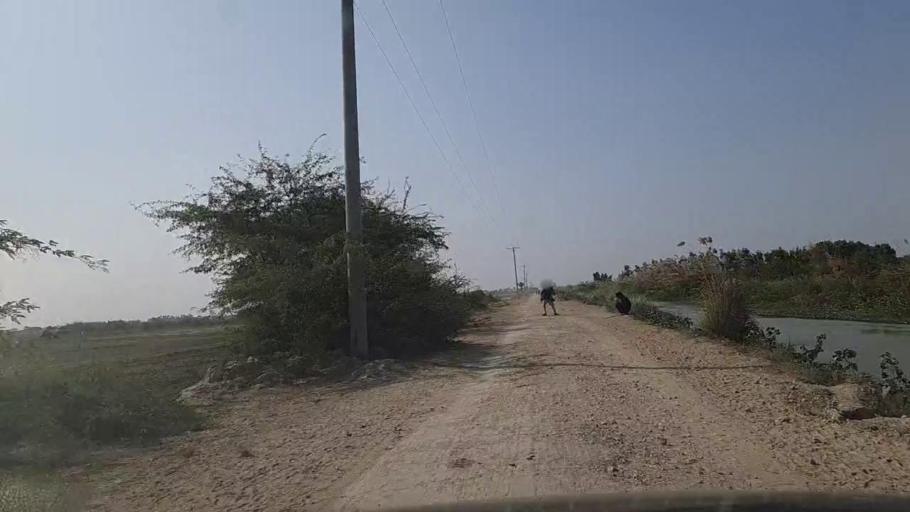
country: PK
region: Sindh
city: Gharo
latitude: 24.6852
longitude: 67.6028
